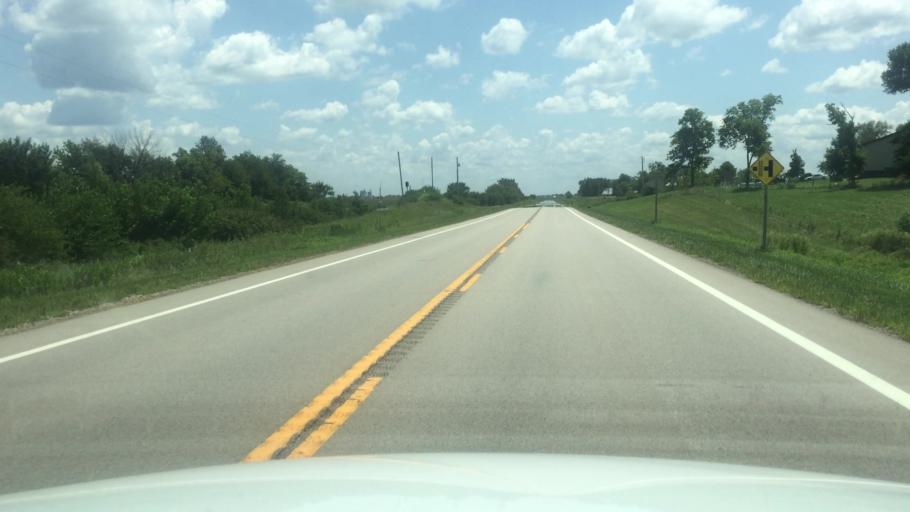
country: US
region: Kansas
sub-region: Brown County
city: Horton
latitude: 39.6068
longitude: -95.3418
